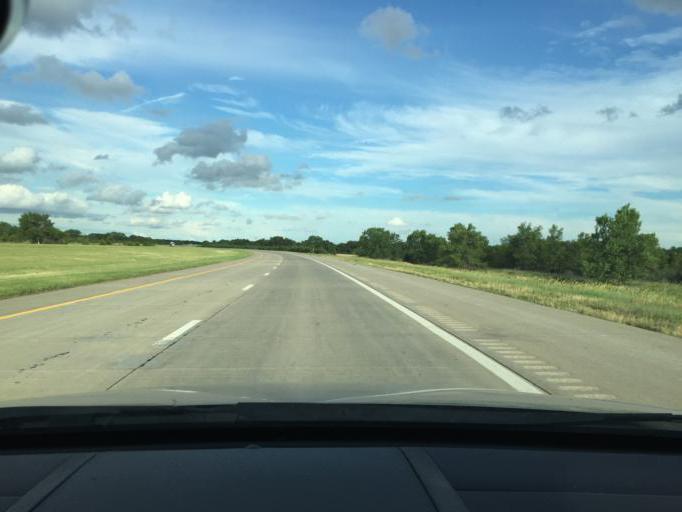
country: US
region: Kansas
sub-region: Reno County
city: South Hutchinson
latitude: 37.9690
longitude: -97.9338
